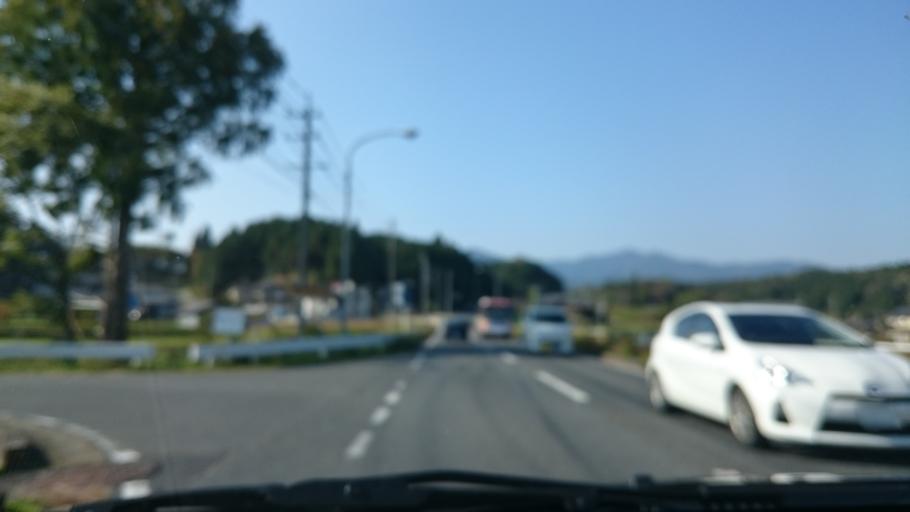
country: JP
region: Gifu
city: Nakatsugawa
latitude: 35.5273
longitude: 137.4661
